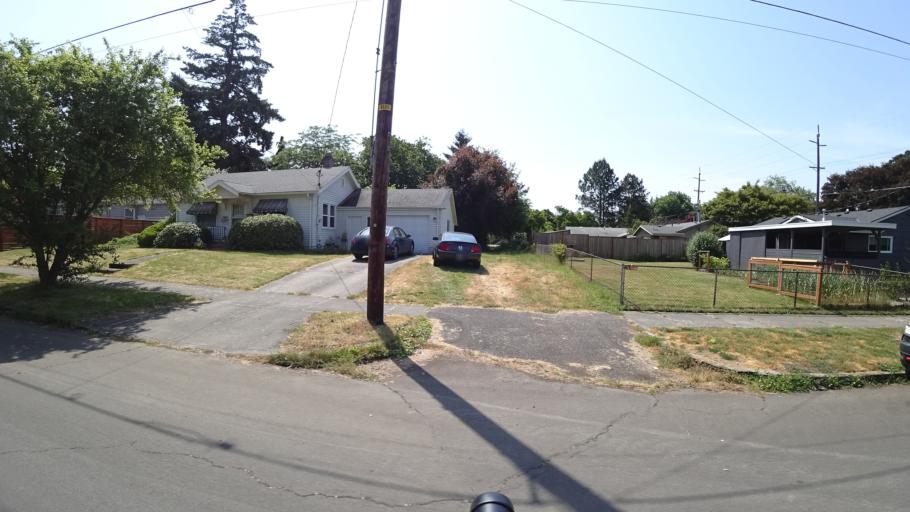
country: US
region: Oregon
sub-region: Multnomah County
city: Portland
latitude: 45.5836
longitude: -122.7053
